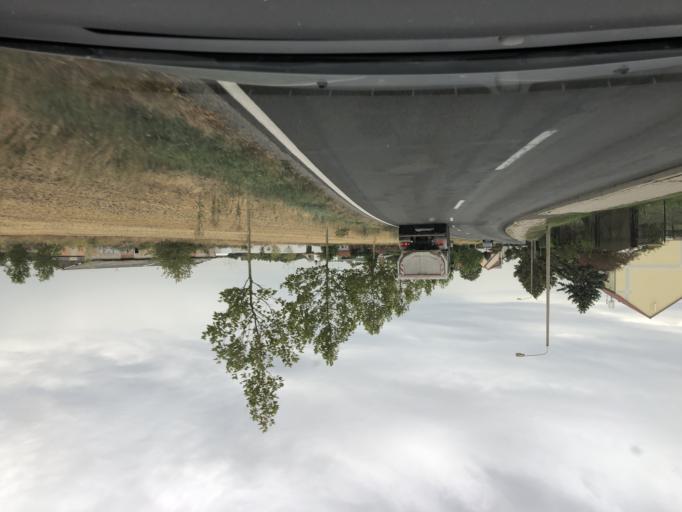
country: DE
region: Saxony-Anhalt
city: Brumby
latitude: 51.8487
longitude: 11.7148
